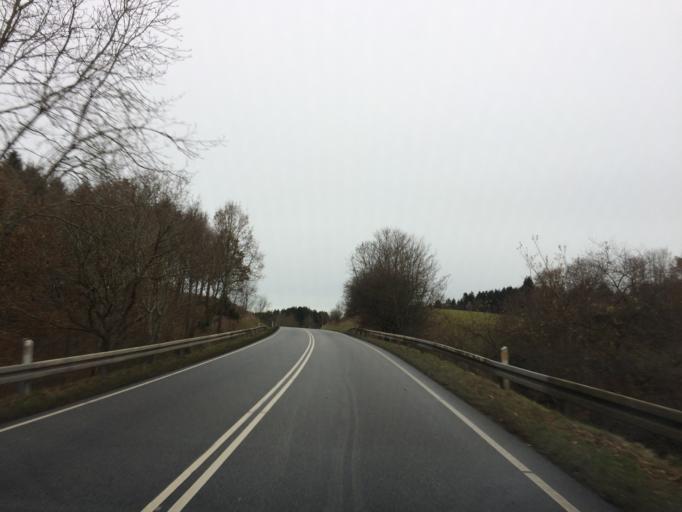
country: DK
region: Zealand
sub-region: Holbaek Kommune
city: Jyderup
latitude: 55.6147
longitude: 11.3909
